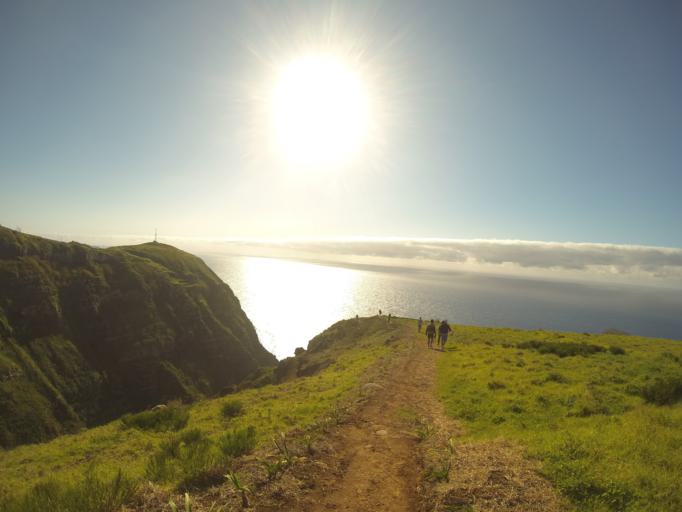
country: PT
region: Madeira
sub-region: Calheta
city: Faja da Ovelha
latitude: 32.8201
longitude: -17.2507
